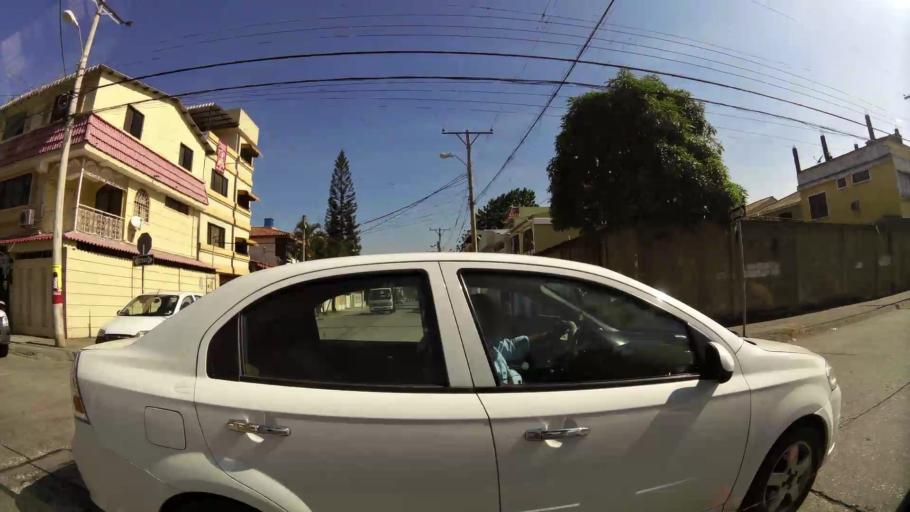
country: EC
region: Guayas
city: Eloy Alfaro
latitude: -2.1470
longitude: -79.9021
